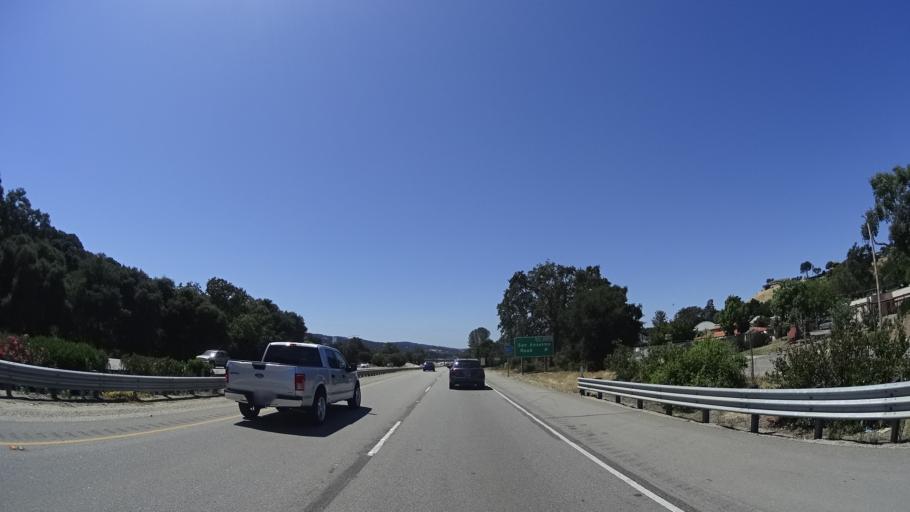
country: US
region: California
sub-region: San Luis Obispo County
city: Atascadero
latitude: 35.4943
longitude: -120.6788
